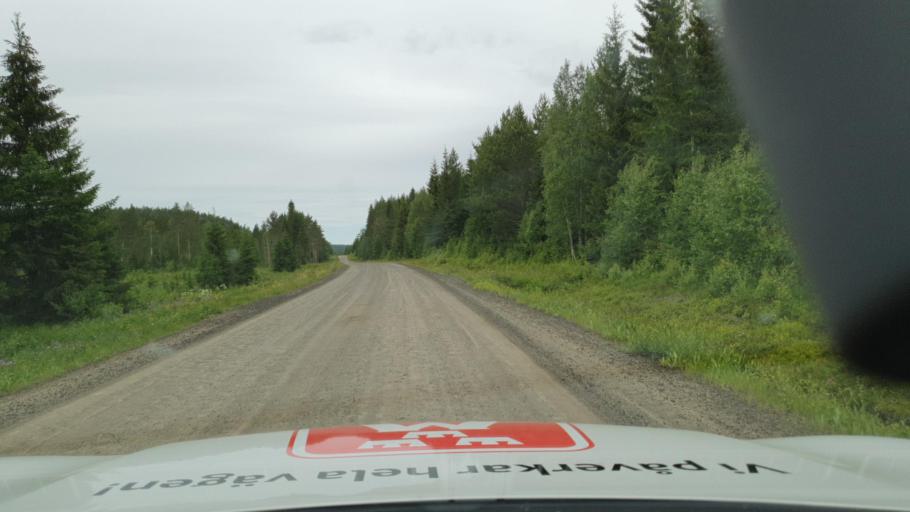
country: SE
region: Vaesterbotten
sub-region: Skelleftea Kommun
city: Burtraesk
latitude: 64.3242
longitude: 20.6344
